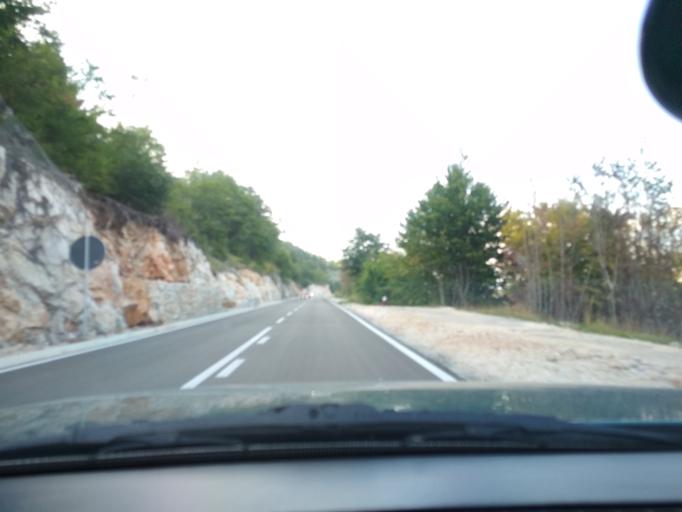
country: ME
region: Cetinje
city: Cetinje
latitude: 42.4309
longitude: 18.8588
